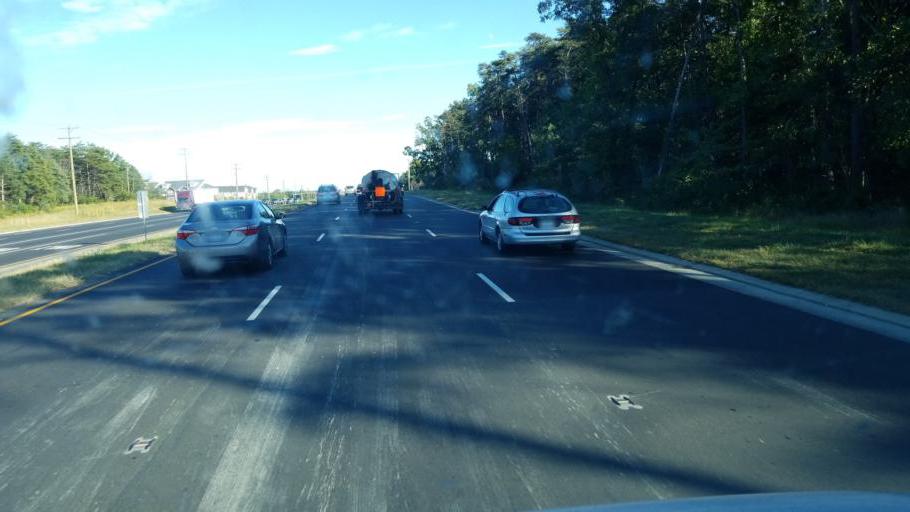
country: US
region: Virginia
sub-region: Loudoun County
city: South Riding
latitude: 38.9363
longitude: -77.5373
